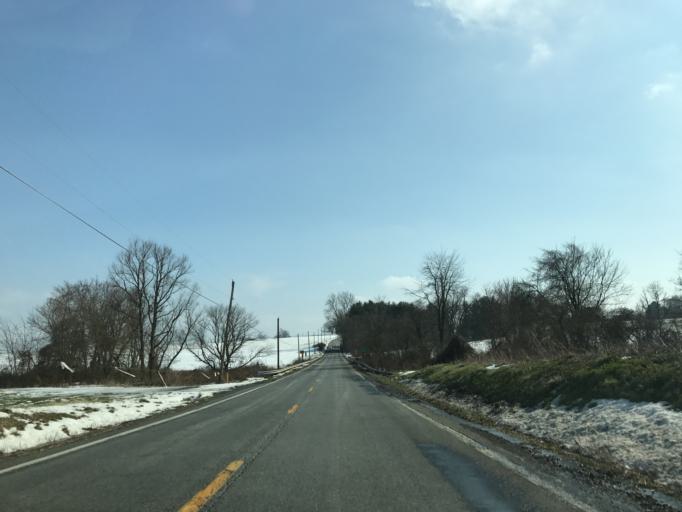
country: US
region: Pennsylvania
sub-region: York County
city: Susquehanna Trails
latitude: 39.6975
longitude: -76.3906
